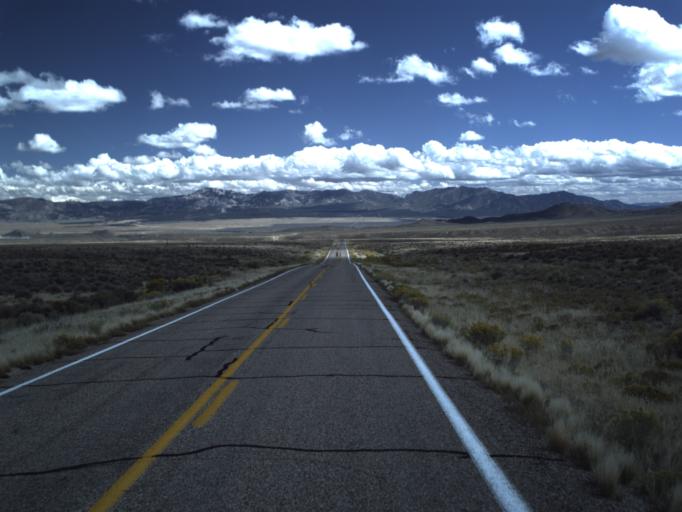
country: US
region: Utah
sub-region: Beaver County
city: Milford
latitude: 38.4468
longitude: -113.1862
